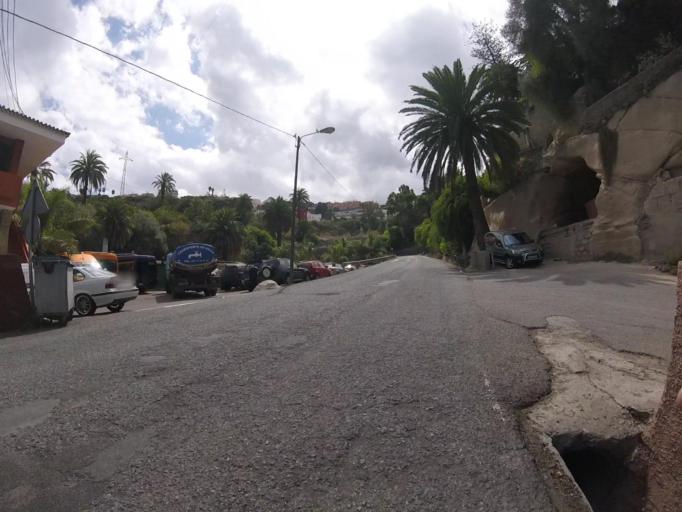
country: ES
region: Canary Islands
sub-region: Provincia de Las Palmas
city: Santa Brigida
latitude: 28.0580
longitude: -15.4657
